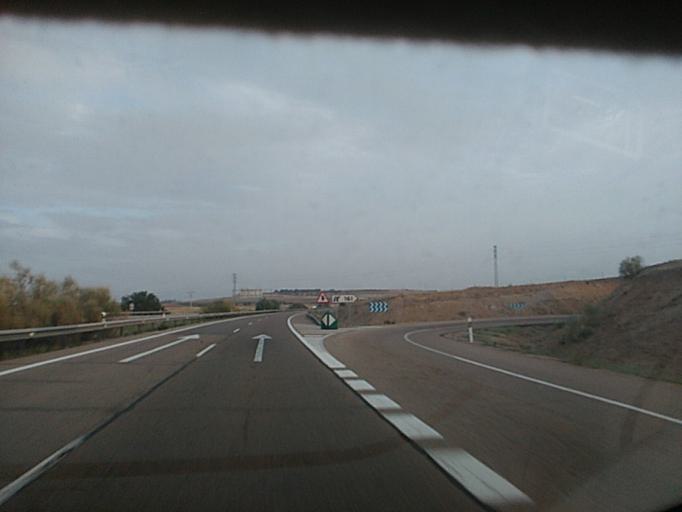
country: ES
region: Castille and Leon
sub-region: Provincia de Valladolid
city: Medina del Campo
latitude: 41.3313
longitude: -4.9295
